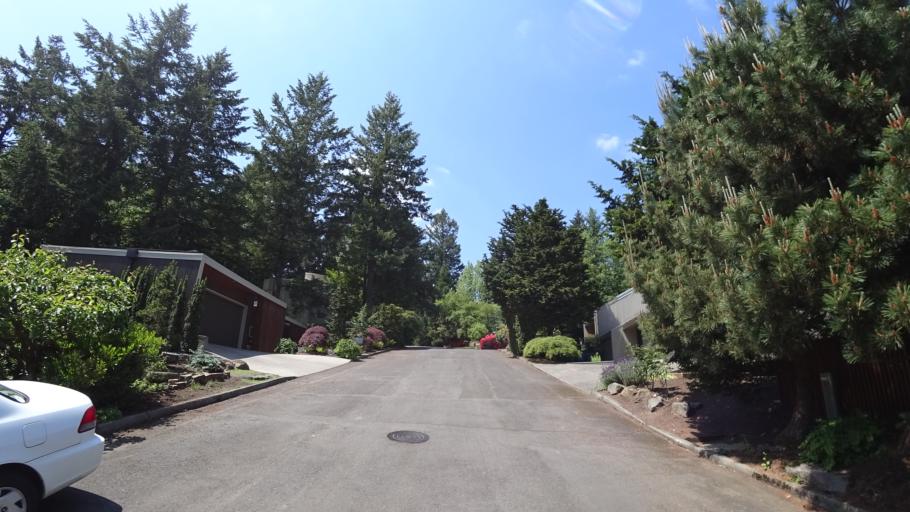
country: US
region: Oregon
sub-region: Multnomah County
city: Portland
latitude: 45.5149
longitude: -122.7124
